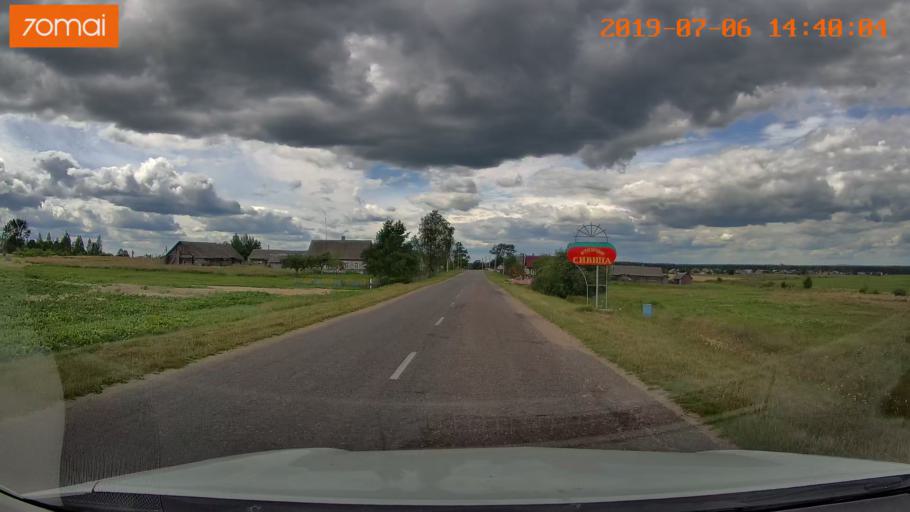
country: BY
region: Minsk
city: Ivyanyets
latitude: 53.9219
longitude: 26.6782
